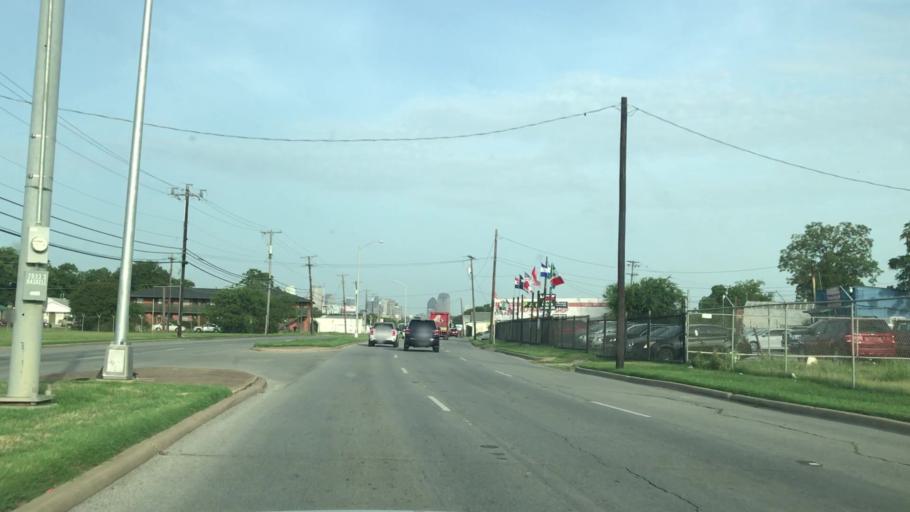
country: US
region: Texas
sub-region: Dallas County
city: Dallas
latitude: 32.7829
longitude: -96.7451
